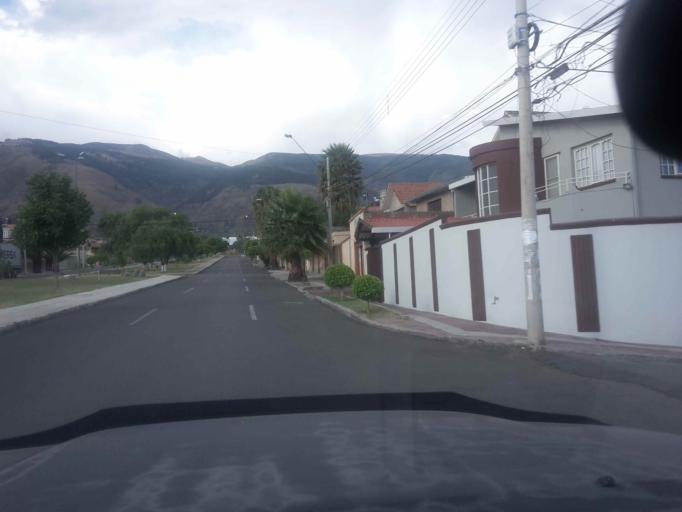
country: BO
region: Cochabamba
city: Cochabamba
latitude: -17.3592
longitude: -66.1698
